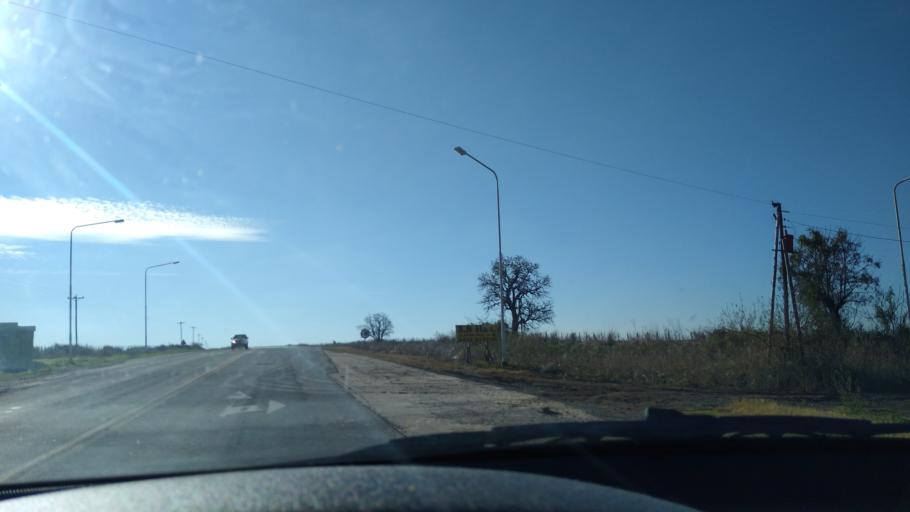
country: AR
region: Entre Rios
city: Aranguren
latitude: -32.4030
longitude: -60.3252
